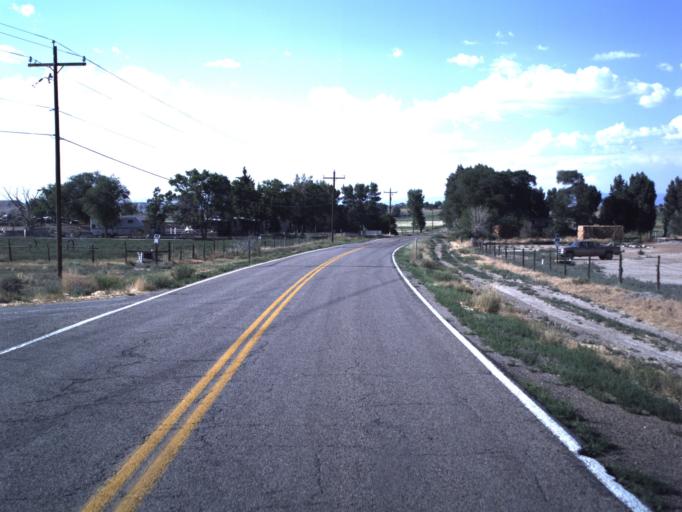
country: US
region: Utah
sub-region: Emery County
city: Huntington
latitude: 39.3728
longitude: -110.8522
